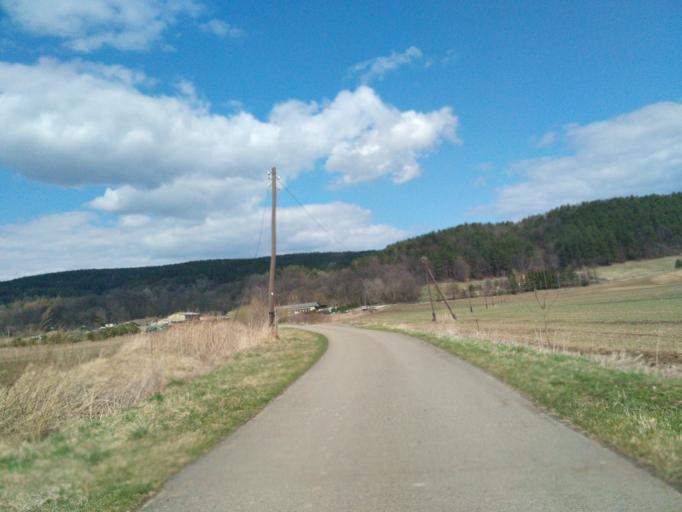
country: PL
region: Subcarpathian Voivodeship
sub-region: Powiat brzozowski
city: Dydnia
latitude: 49.6733
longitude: 22.2669
